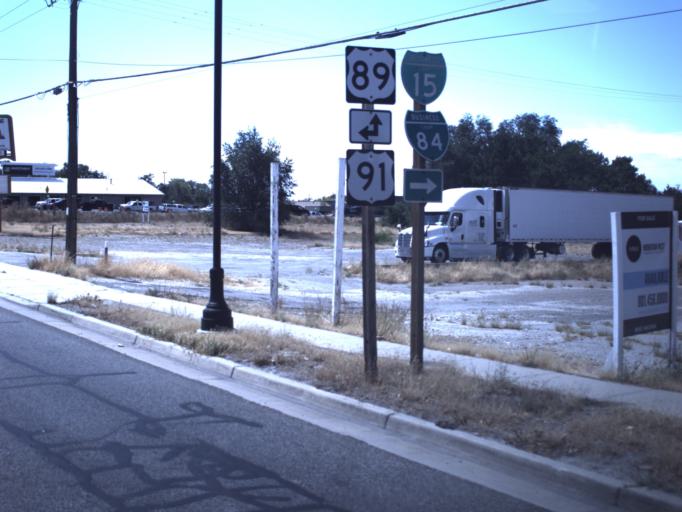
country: US
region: Utah
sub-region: Box Elder County
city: Brigham City
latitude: 41.4876
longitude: -112.0163
